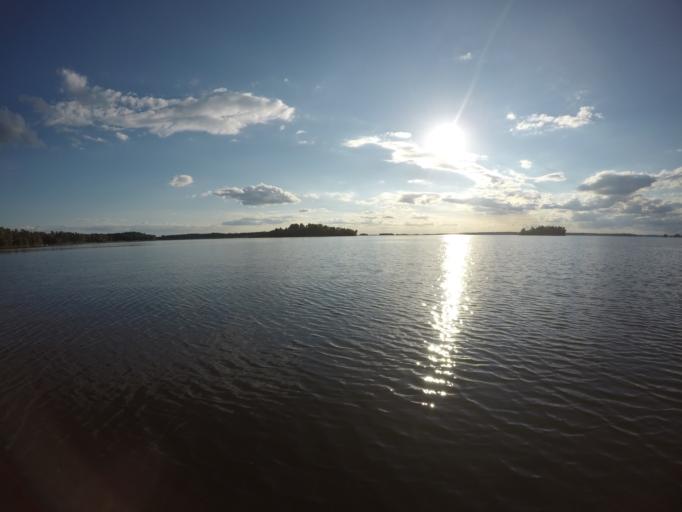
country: SE
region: Soedermanland
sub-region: Eskilstuna Kommun
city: Kvicksund
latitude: 59.4515
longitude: 16.3018
